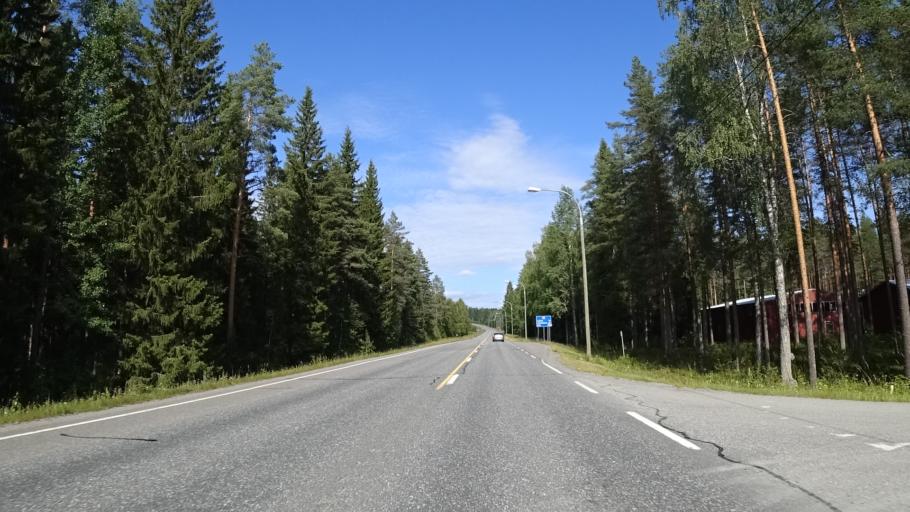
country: FI
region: North Karelia
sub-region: Joensuu
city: Eno
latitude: 62.7760
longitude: 30.0603
